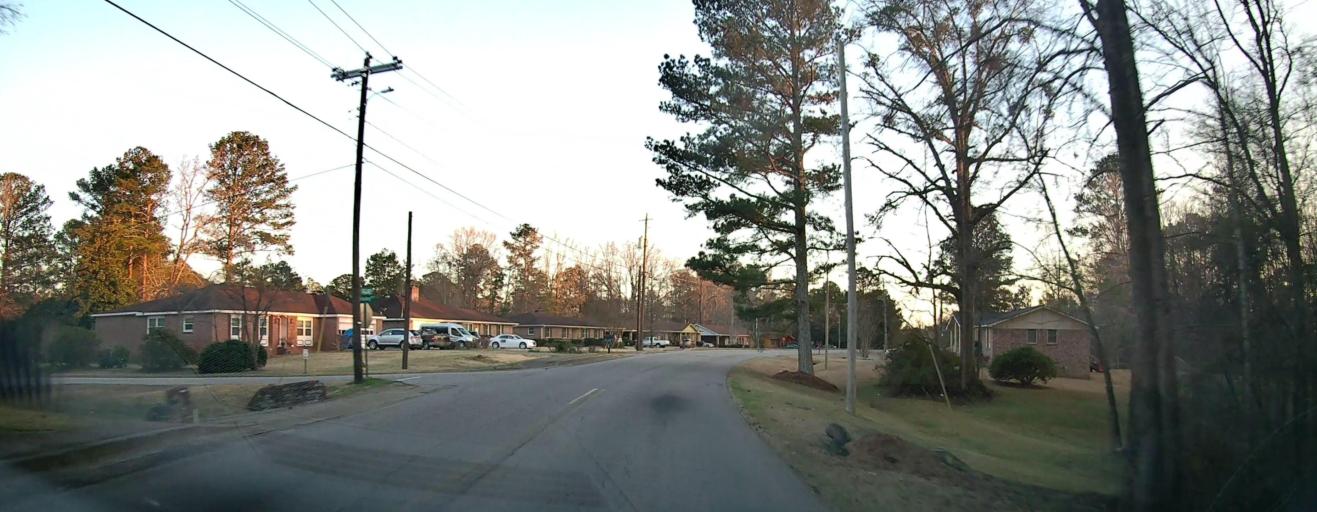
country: US
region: Georgia
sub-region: Troup County
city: La Grange
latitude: 33.0330
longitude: -85.0044
